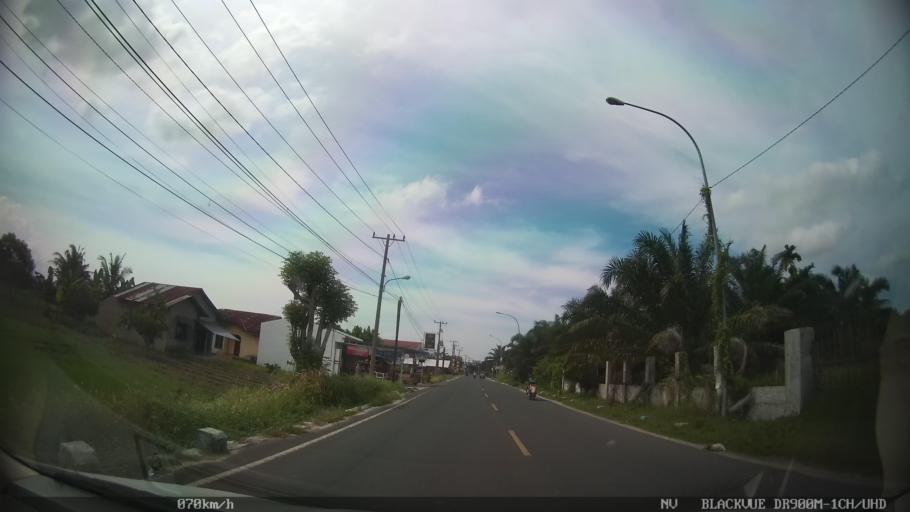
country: ID
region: North Sumatra
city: Percut
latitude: 3.5878
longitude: 98.8602
